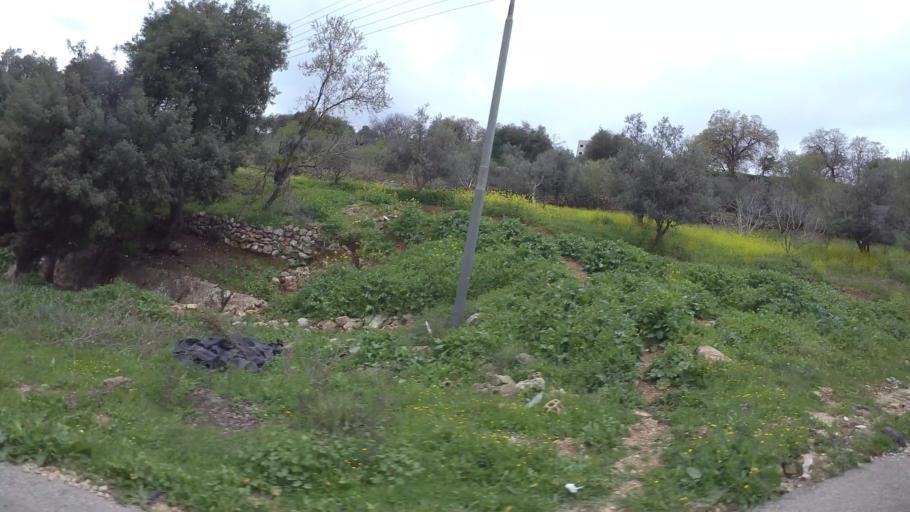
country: JO
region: Amman
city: Wadi as Sir
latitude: 31.9543
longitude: 35.8129
